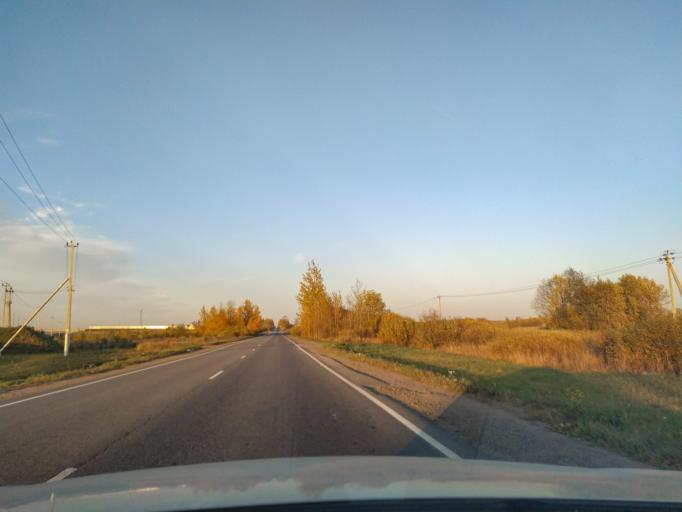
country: RU
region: Leningrad
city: Maloye Verevo
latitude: 59.6045
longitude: 30.1855
